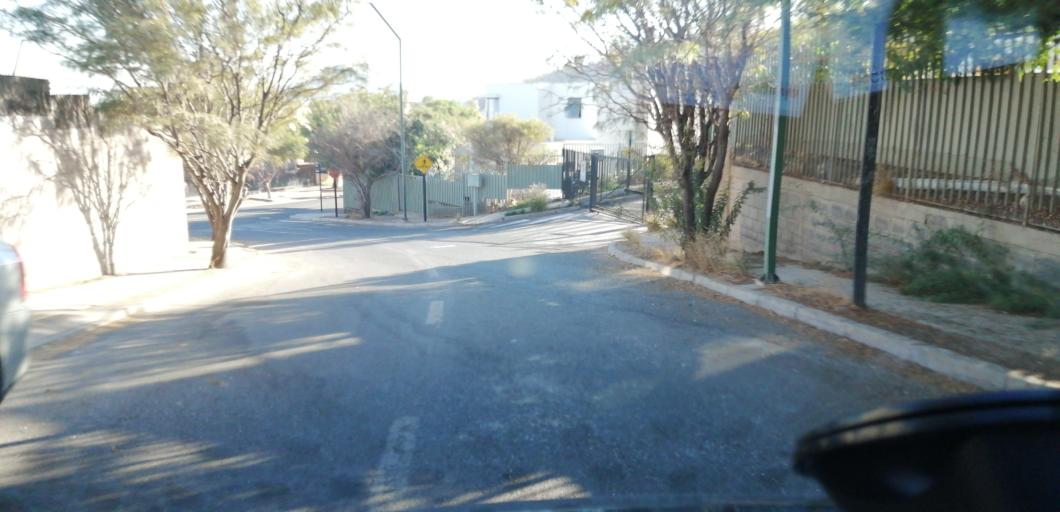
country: CL
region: Santiago Metropolitan
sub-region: Provincia de Santiago
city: Lo Prado
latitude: -33.4515
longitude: -70.8392
